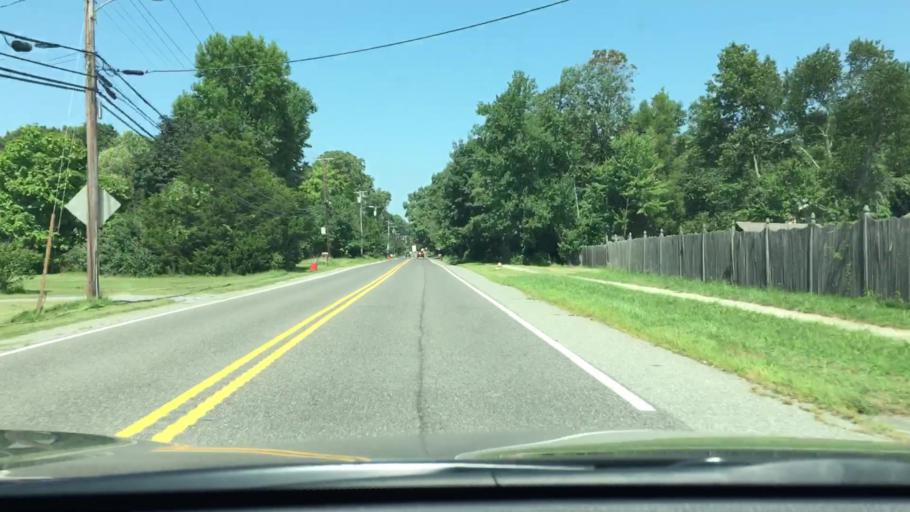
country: US
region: New Jersey
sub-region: Cumberland County
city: Millville
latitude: 39.3820
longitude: -75.0706
